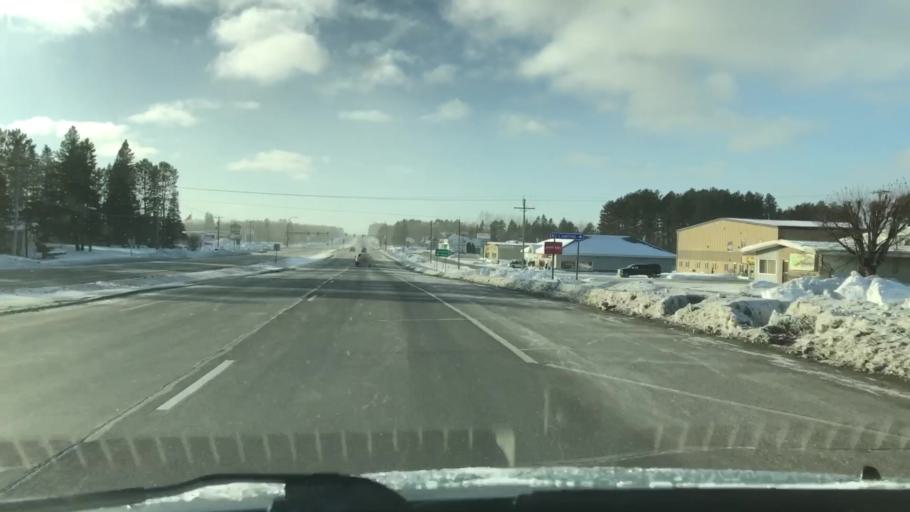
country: US
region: Minnesota
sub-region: Saint Louis County
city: Hermantown
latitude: 46.8368
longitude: -92.2126
